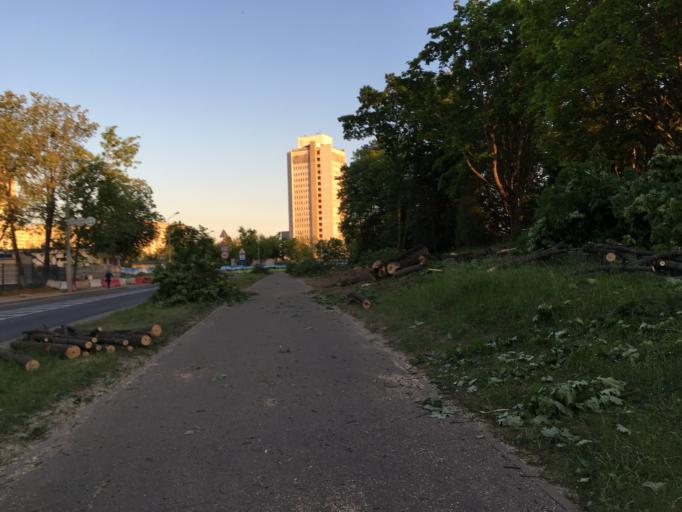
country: BY
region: Minsk
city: Minsk
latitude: 53.9263
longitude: 27.6273
